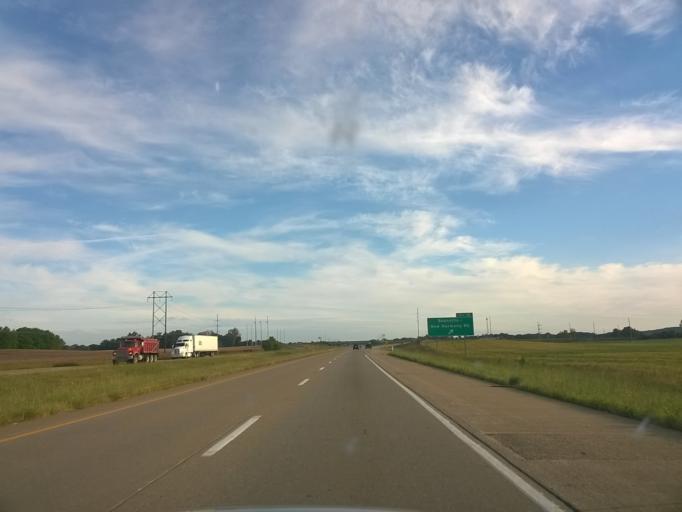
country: US
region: Indiana
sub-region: Vanderburgh County
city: Melody Hill
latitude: 38.0835
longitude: -87.4766
